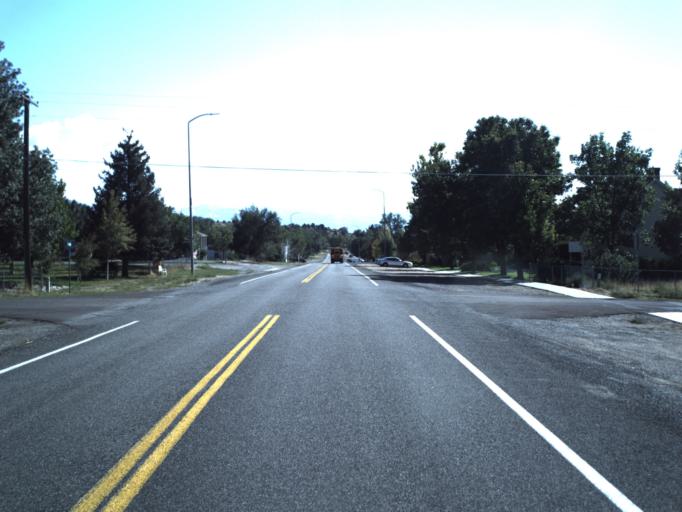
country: US
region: Utah
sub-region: Millard County
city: Fillmore
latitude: 39.1013
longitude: -112.2710
